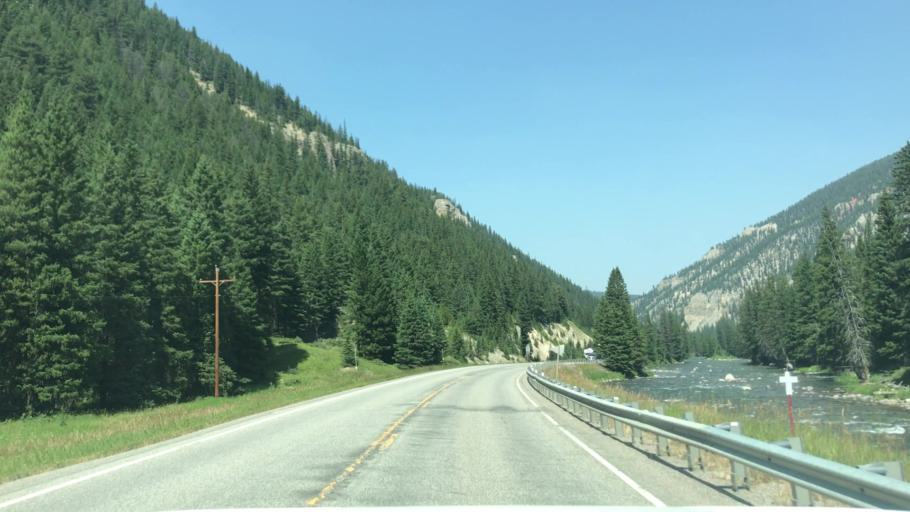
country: US
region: Montana
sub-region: Gallatin County
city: Big Sky
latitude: 45.1269
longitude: -111.2322
